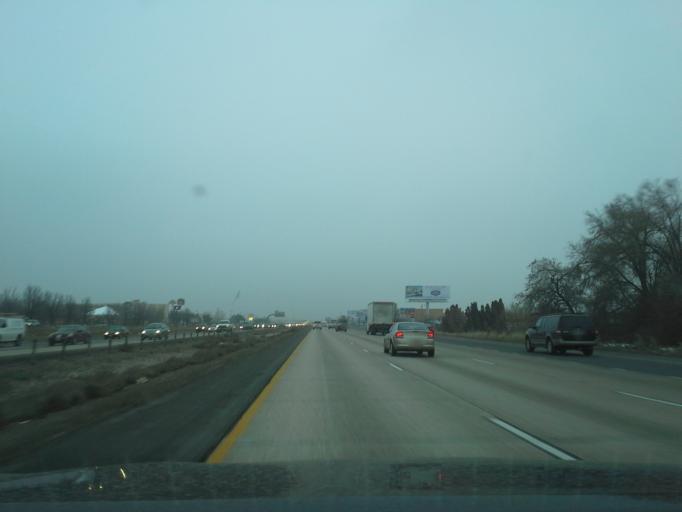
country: US
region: Utah
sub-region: Davis County
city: Layton
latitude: 41.0831
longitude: -111.9853
